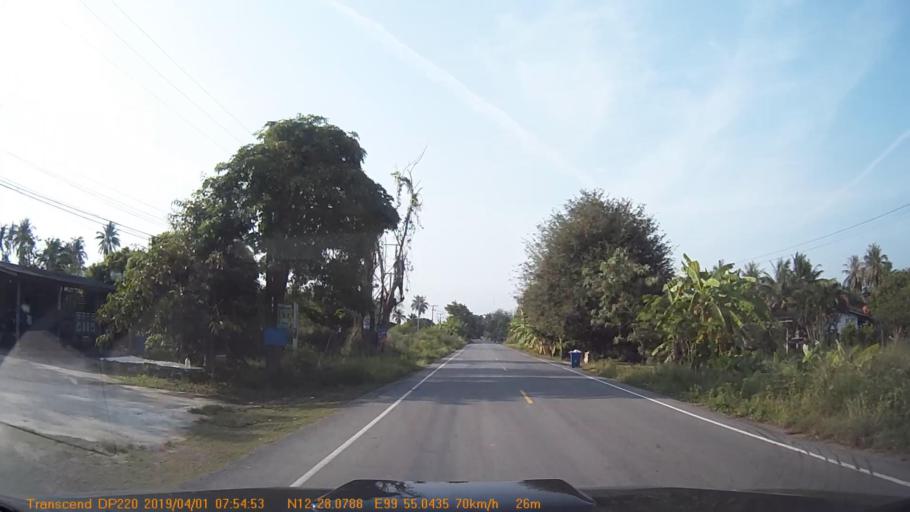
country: TH
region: Prachuap Khiri Khan
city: Pran Buri
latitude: 12.4676
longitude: 99.9174
